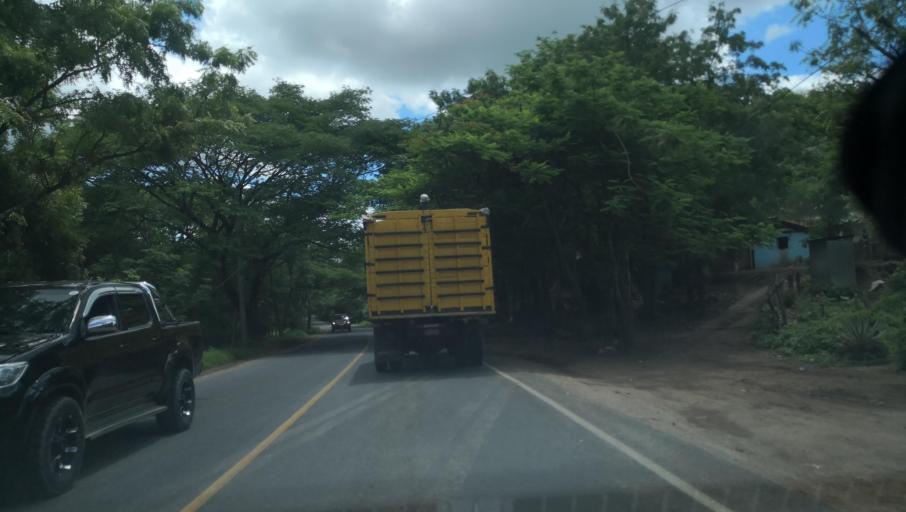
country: NI
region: Madriz
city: Yalaguina
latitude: 13.4763
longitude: -86.4823
